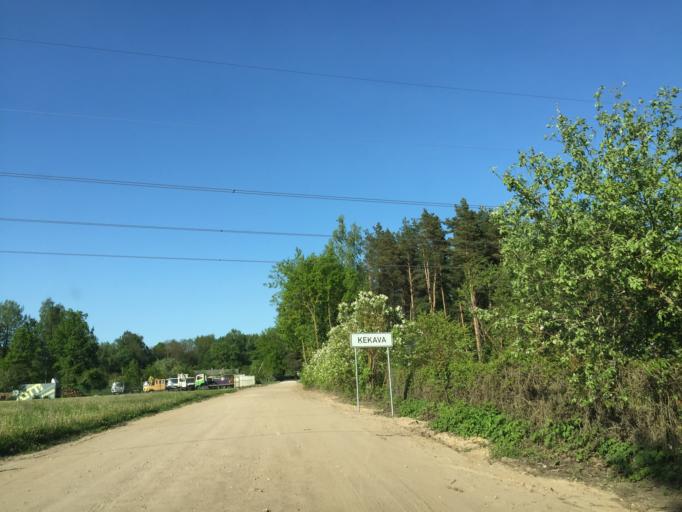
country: LV
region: Kekava
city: Kekava
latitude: 56.8191
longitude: 24.2340
